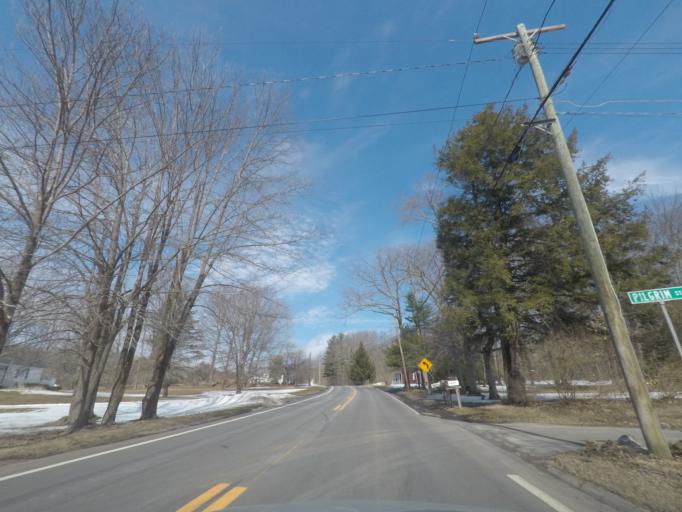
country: US
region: Massachusetts
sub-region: Berkshire County
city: West Stockbridge
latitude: 42.3561
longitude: -73.3813
